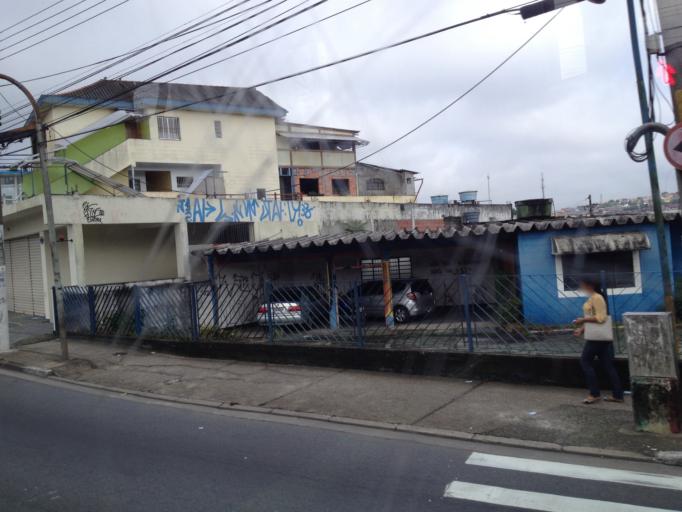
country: BR
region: Sao Paulo
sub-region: Taboao Da Serra
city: Taboao da Serra
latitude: -23.6438
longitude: -46.7427
